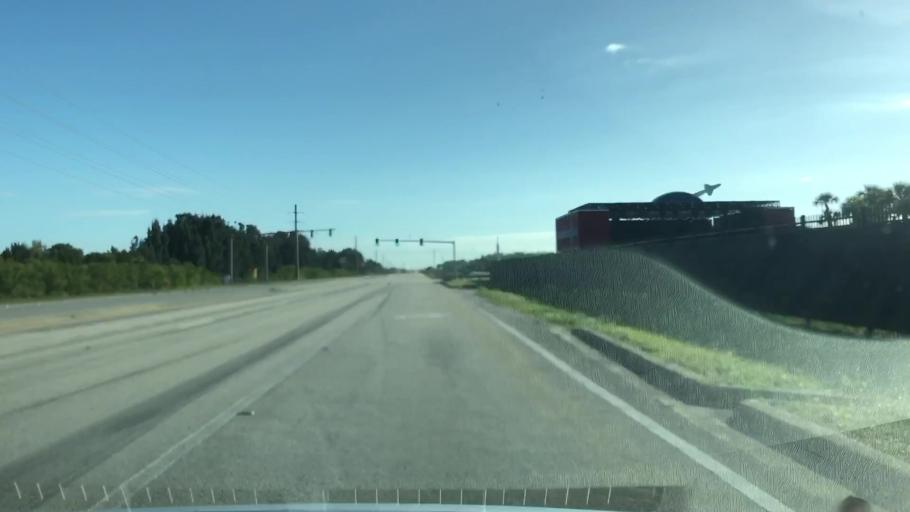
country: US
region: Florida
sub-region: Brevard County
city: Merritt Island
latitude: 28.5260
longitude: -80.6803
